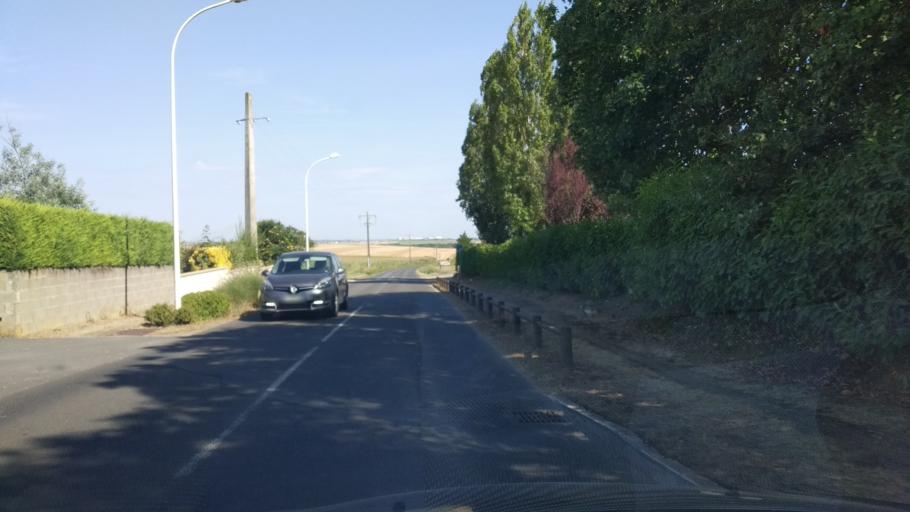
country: FR
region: Poitou-Charentes
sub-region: Departement de la Vienne
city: Cisse
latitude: 46.6358
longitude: 0.2470
